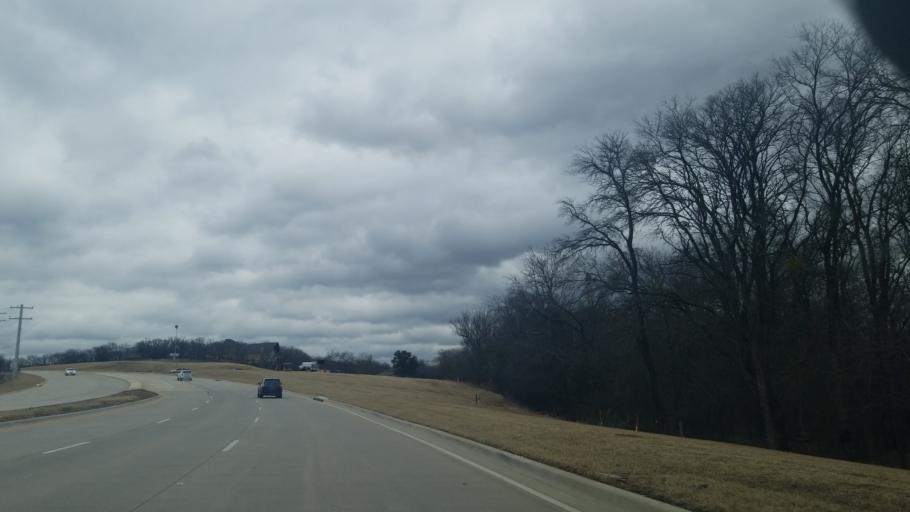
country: US
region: Texas
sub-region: Denton County
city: Trophy Club
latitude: 33.0473
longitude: -97.1777
